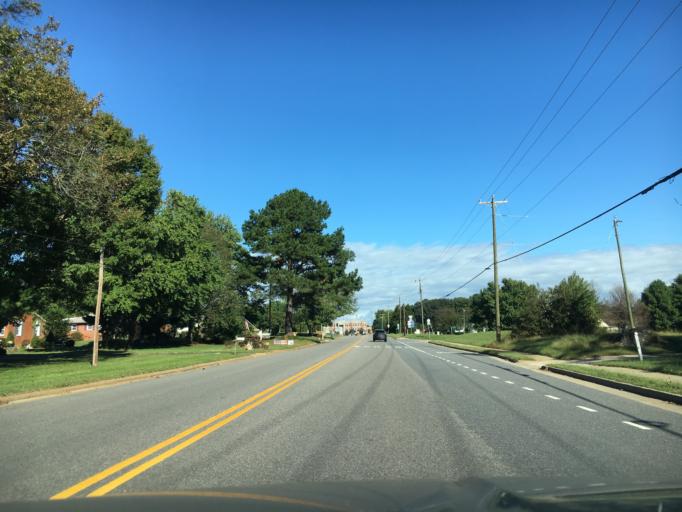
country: US
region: Virginia
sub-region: Goochland County
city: Goochland
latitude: 37.6900
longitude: -77.8862
